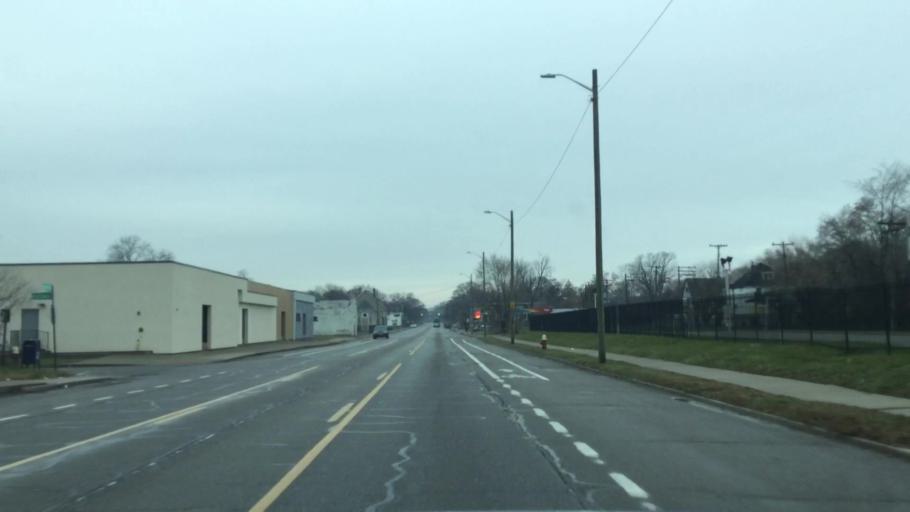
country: US
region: Michigan
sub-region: Wayne County
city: Detroit
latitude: 42.3574
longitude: -83.0025
